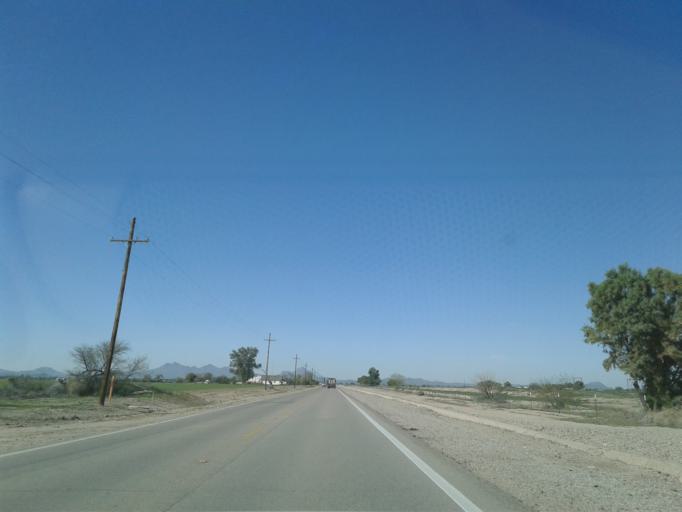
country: US
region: Arizona
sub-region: Pima County
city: Marana
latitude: 32.4605
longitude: -111.2423
